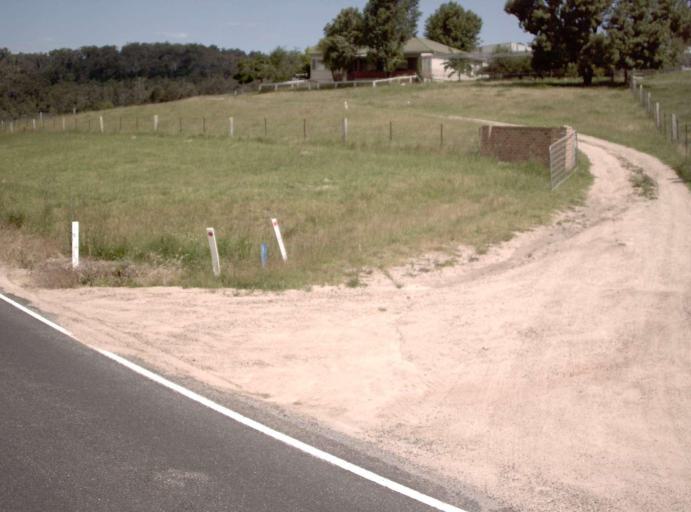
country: AU
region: New South Wales
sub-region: Bega Valley
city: Eden
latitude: -37.4757
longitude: 149.5945
